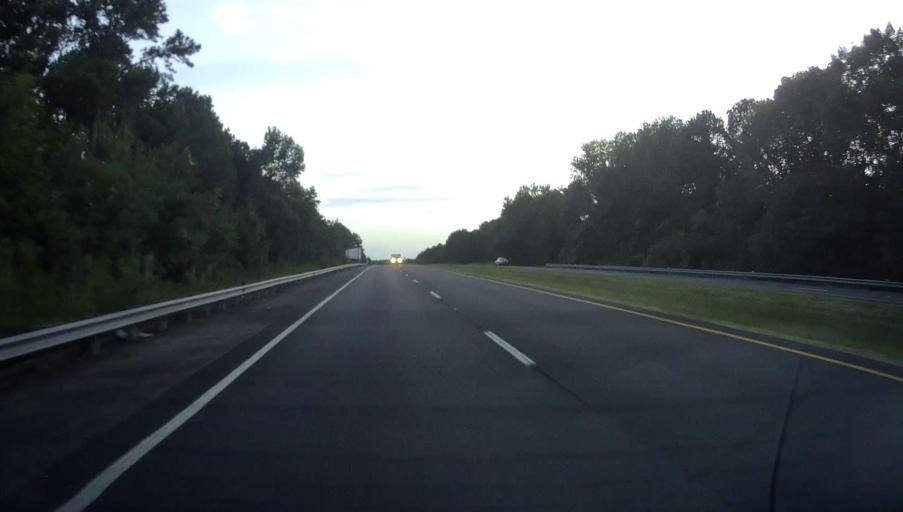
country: US
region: Georgia
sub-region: Muscogee County
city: Columbus
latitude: 32.5296
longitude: -84.8834
